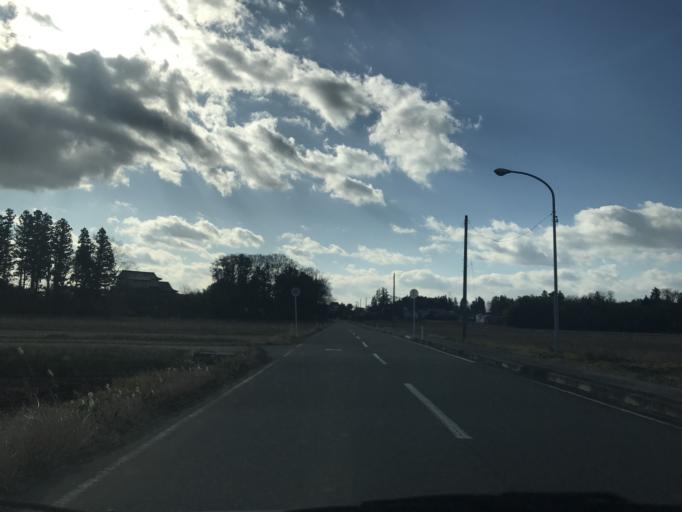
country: JP
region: Iwate
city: Ichinoseki
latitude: 38.7636
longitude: 141.0593
